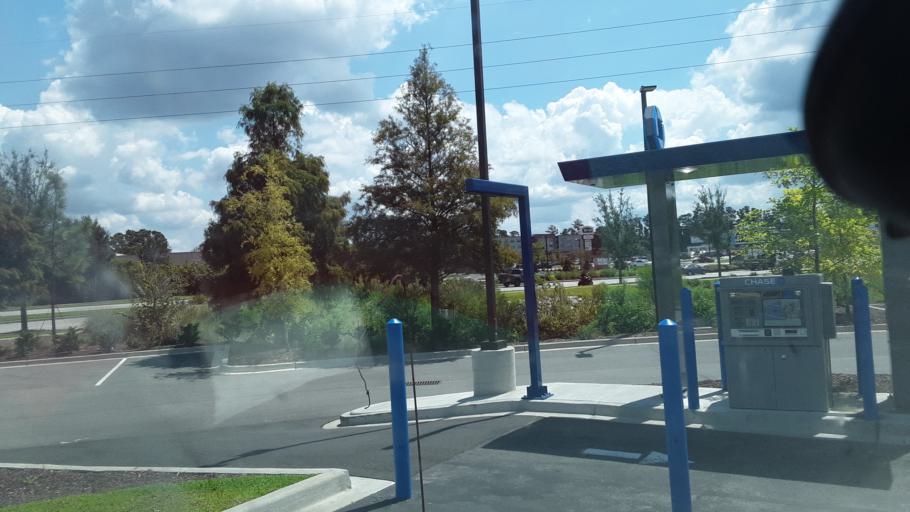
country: US
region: South Carolina
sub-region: Berkeley County
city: Sangaree
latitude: 33.0411
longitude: -80.1399
